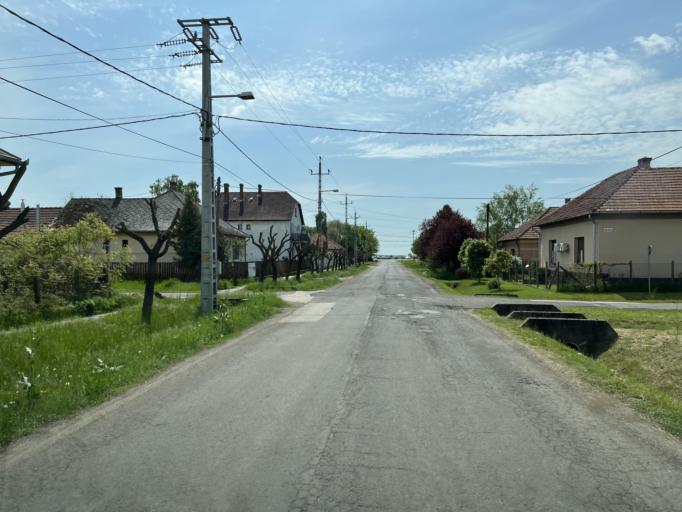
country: HU
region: Pest
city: Tapiogyorgye
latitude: 47.3270
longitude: 19.9505
